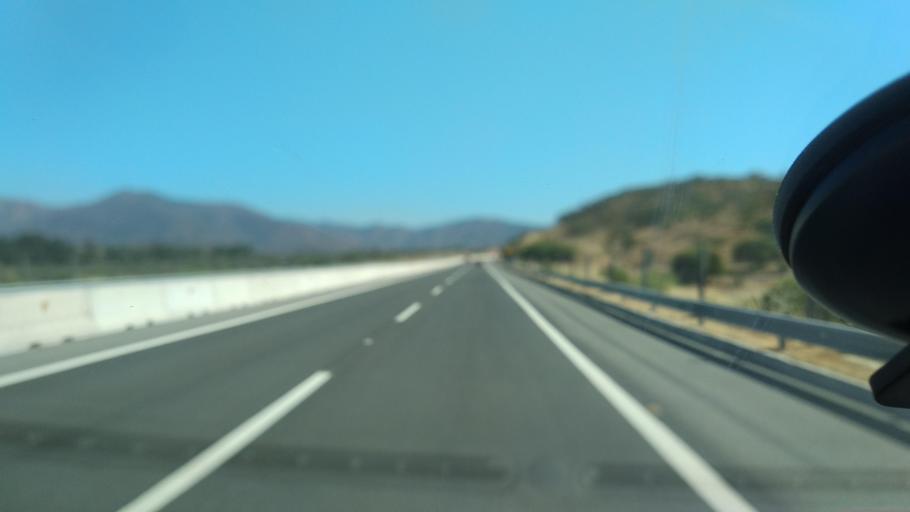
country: CL
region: Valparaiso
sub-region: Provincia de Marga Marga
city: Limache
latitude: -33.0211
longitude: -71.3197
